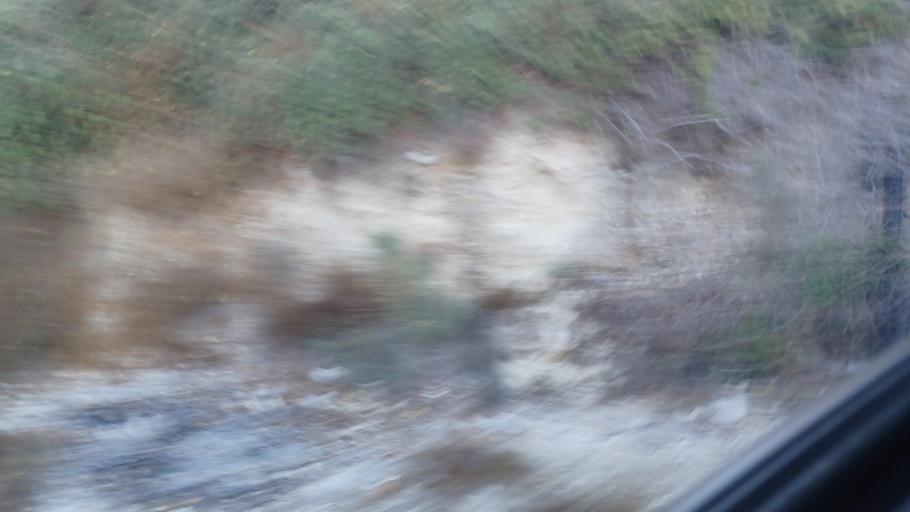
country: CY
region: Pafos
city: Tala
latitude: 34.8669
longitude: 32.4550
